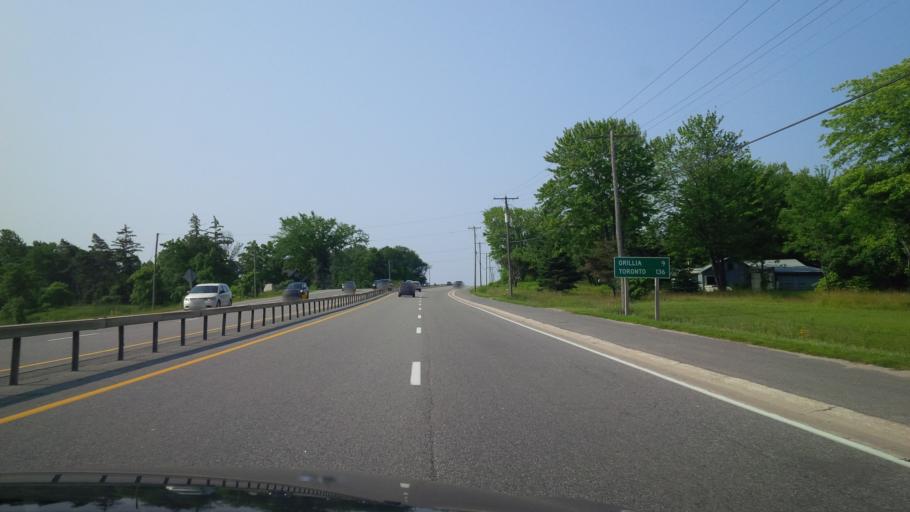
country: CA
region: Ontario
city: Orillia
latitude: 44.6675
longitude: -79.4120
